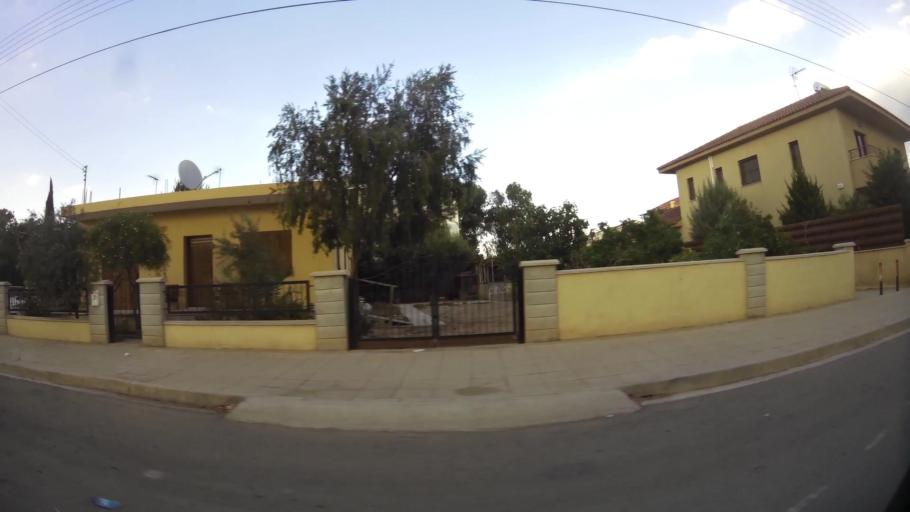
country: CY
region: Lefkosia
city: Tseri
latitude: 35.1140
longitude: 33.3152
